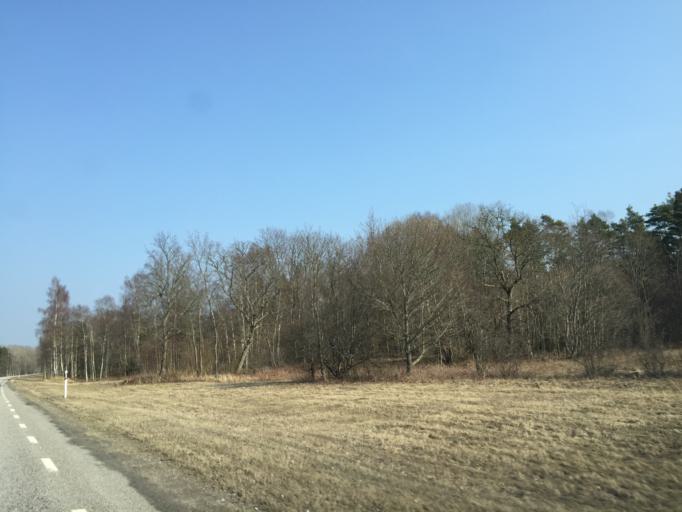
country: EE
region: Saare
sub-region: Kuressaare linn
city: Kuressaare
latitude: 58.3956
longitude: 22.7544
